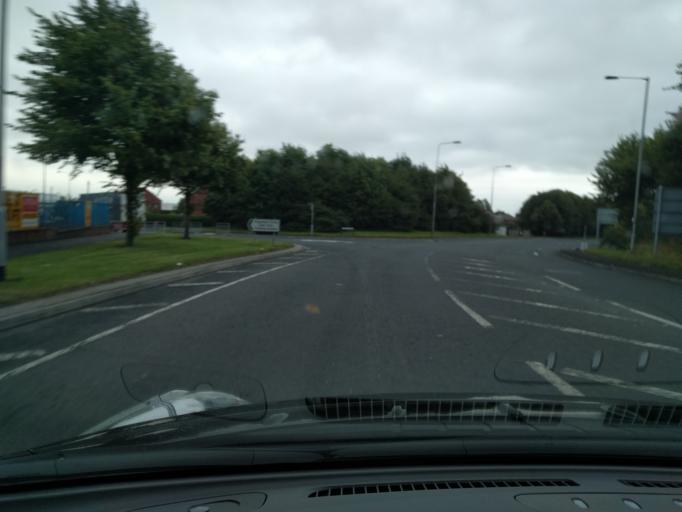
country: GB
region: England
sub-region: Borough of Wigan
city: Ashton in Makerfield
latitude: 53.4748
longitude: -2.6558
